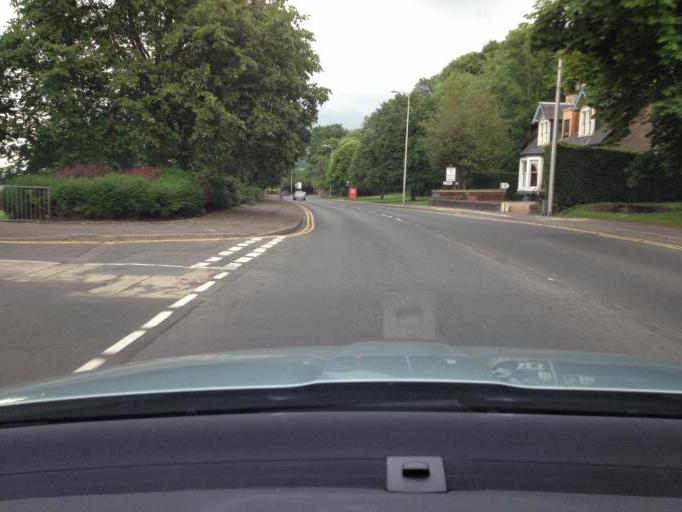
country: GB
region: Scotland
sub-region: Perth and Kinross
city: Perth
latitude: 56.3775
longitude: -3.4327
